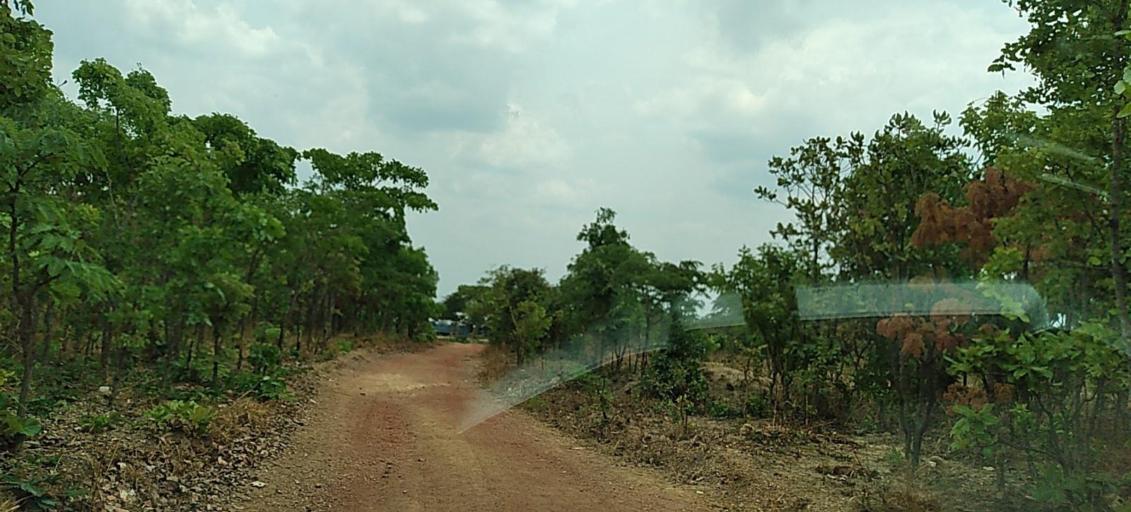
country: ZM
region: Copperbelt
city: Chililabombwe
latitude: -12.3122
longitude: 27.7911
